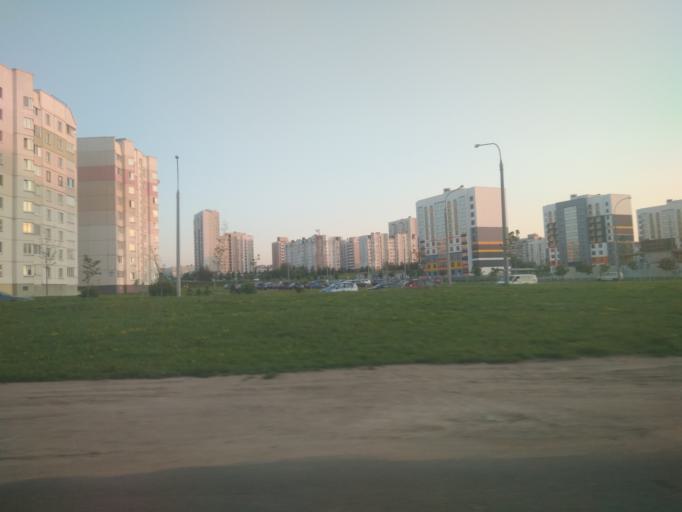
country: BY
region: Minsk
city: Zhdanovichy
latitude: 53.9226
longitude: 27.4578
